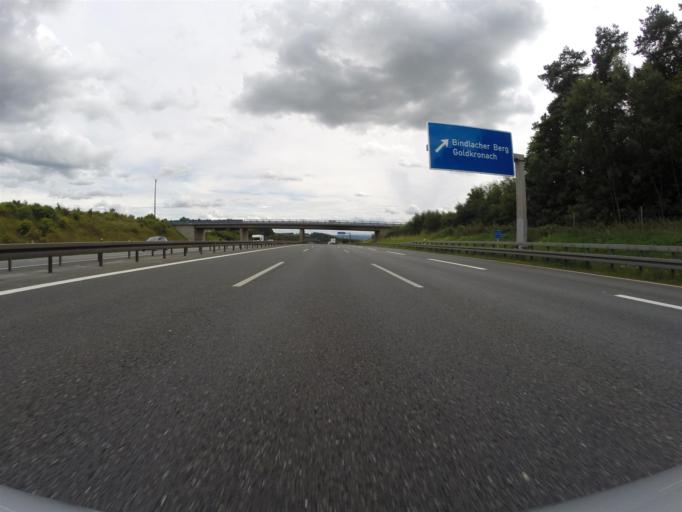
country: DE
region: Bavaria
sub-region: Upper Franconia
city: Bindlach
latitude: 50.0157
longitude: 11.6054
